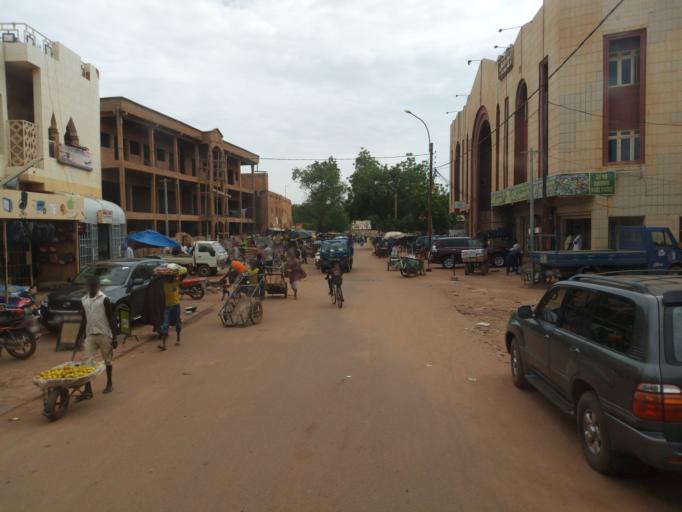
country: NE
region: Niamey
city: Niamey
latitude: 13.5205
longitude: 2.1155
